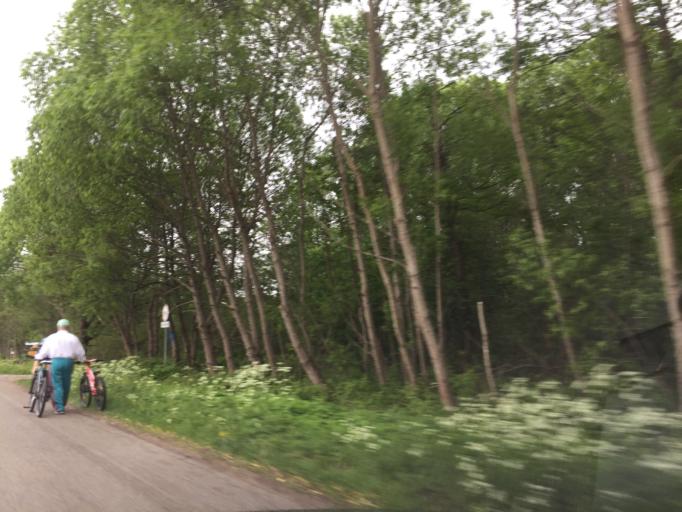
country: LT
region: Klaipedos apskritis
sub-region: Klaipeda
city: Klaipeda
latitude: 55.8098
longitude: 21.0729
